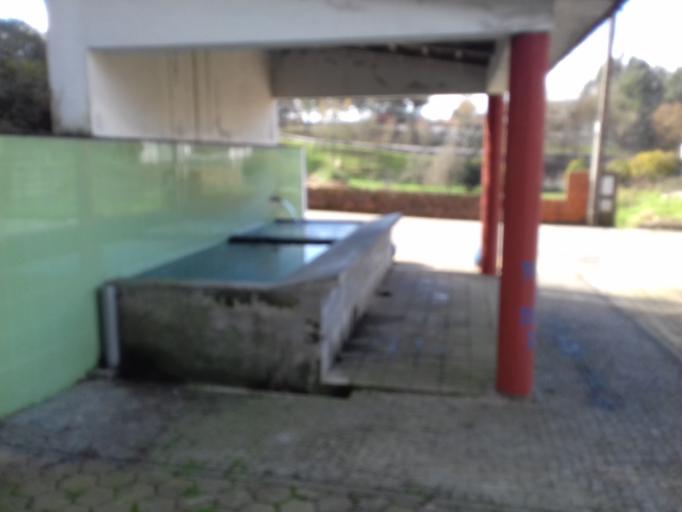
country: PT
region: Aveiro
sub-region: Albergaria-A-Velha
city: Branca
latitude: 40.7682
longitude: -8.4857
